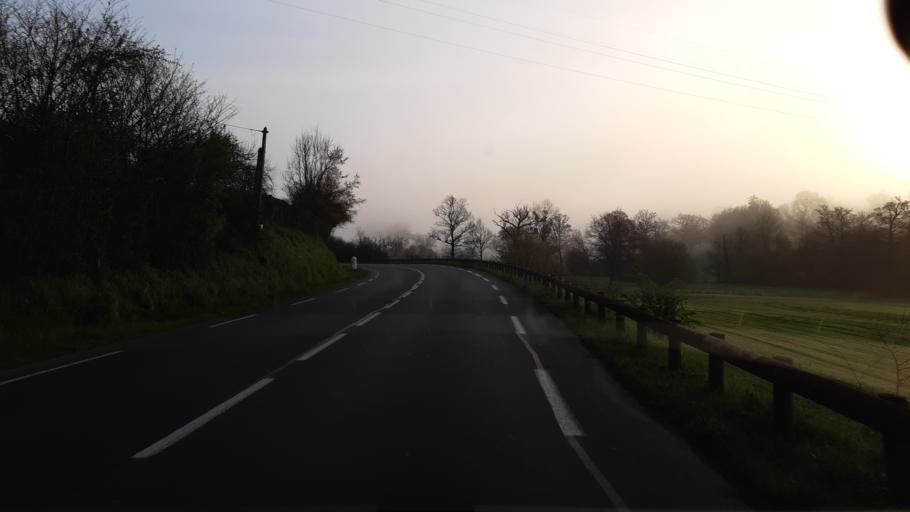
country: FR
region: Lower Normandy
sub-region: Departement de la Manche
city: Agneaux
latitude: 49.0833
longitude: -1.1170
